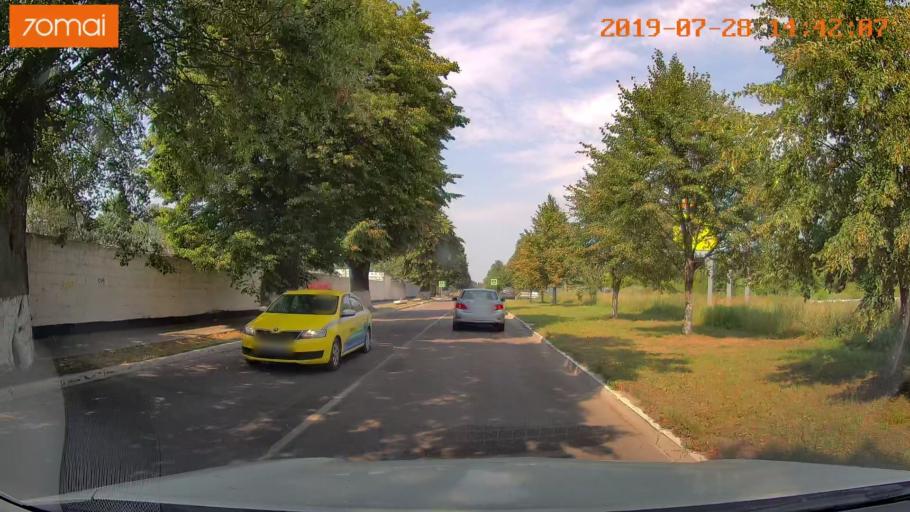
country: RU
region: Kaliningrad
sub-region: Gorod Kaliningrad
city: Yantarnyy
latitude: 54.8581
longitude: 19.9433
